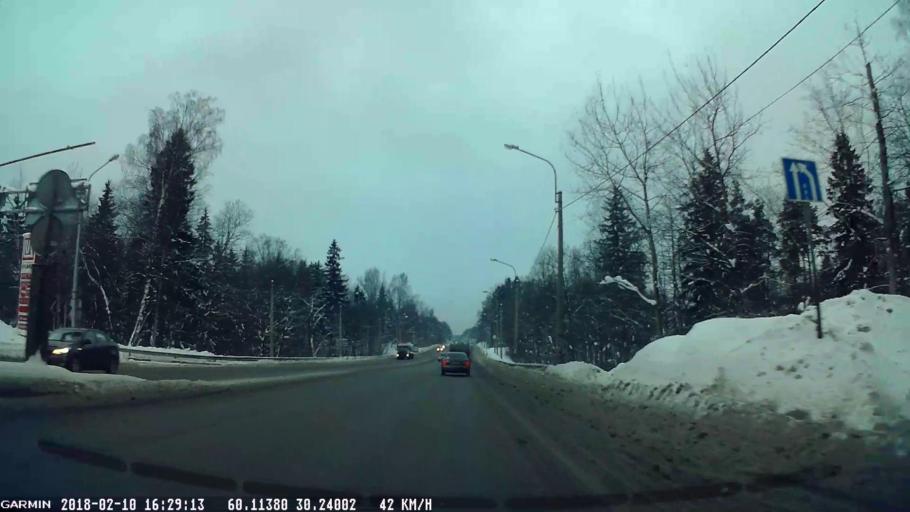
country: RU
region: St.-Petersburg
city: Levashovo
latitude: 60.1142
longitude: 30.2395
